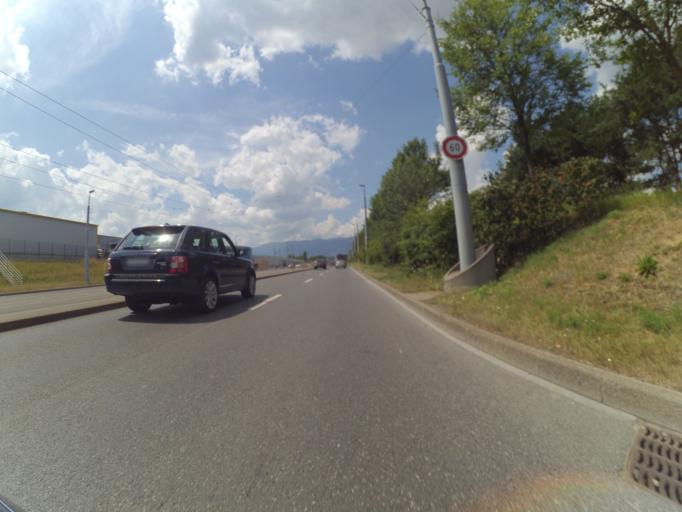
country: CH
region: Geneva
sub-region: Geneva
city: Vernier
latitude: 46.2234
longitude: 6.0924
